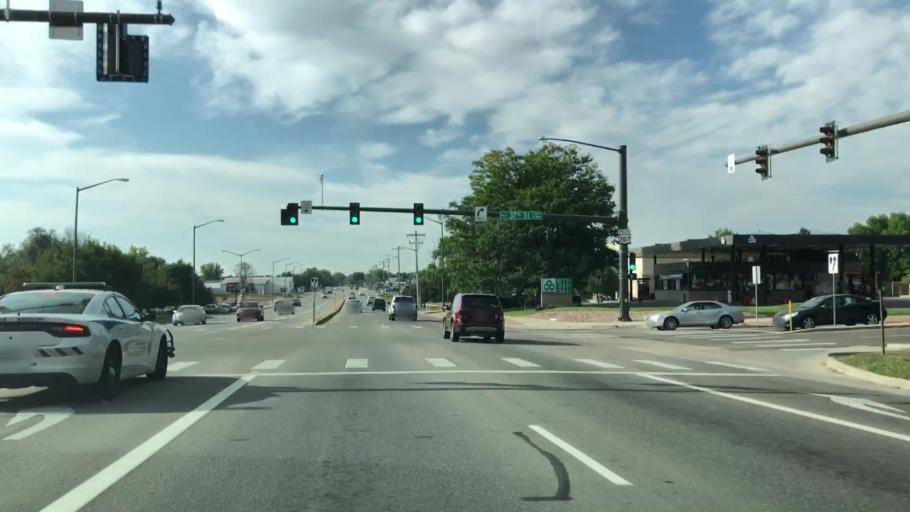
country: US
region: Colorado
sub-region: Larimer County
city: Loveland
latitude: 40.4307
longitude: -105.0775
